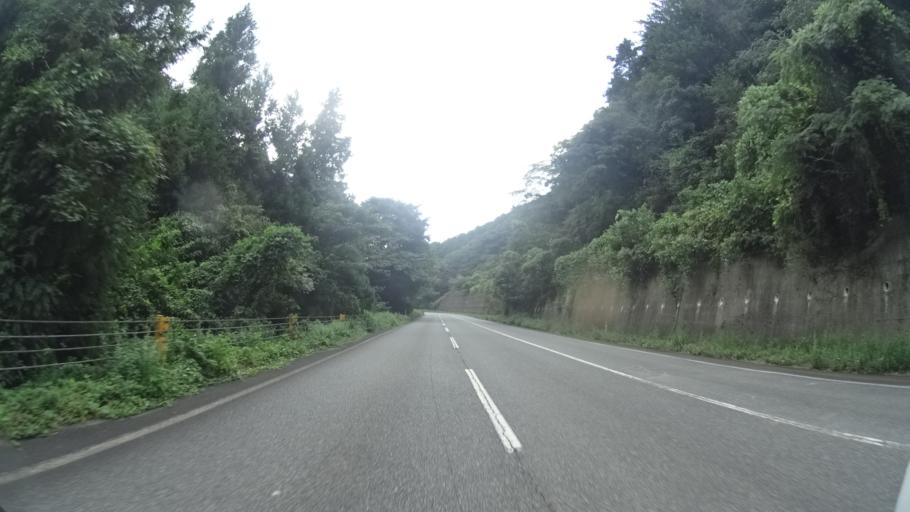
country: JP
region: Yamaguchi
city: Hagi
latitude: 34.5408
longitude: 131.5998
